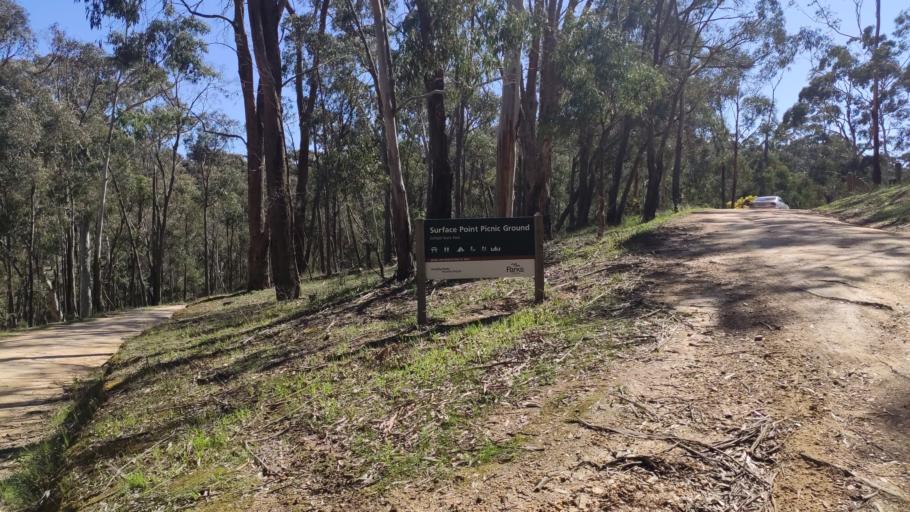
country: AU
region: Victoria
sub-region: Ballarat North
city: Delacombe
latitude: -37.7705
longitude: 143.7385
